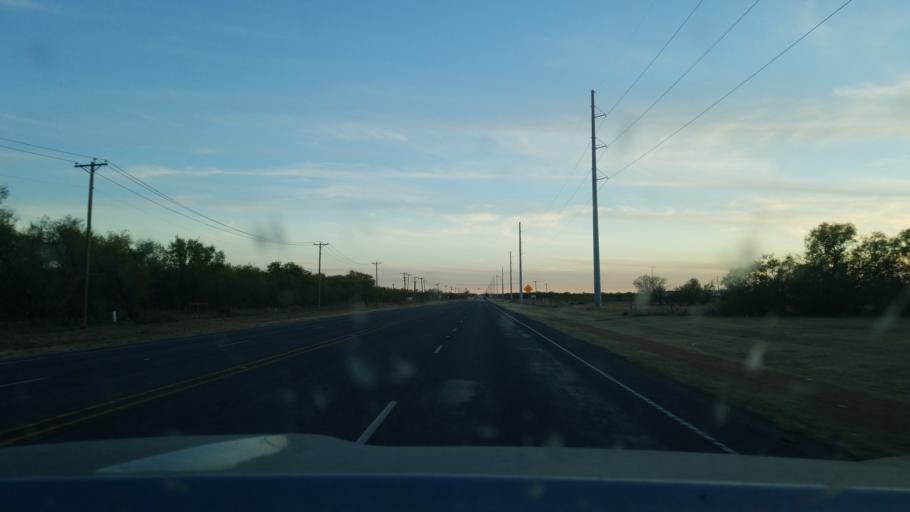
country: US
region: Texas
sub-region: Stephens County
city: Breckenridge
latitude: 32.7334
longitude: -98.9026
